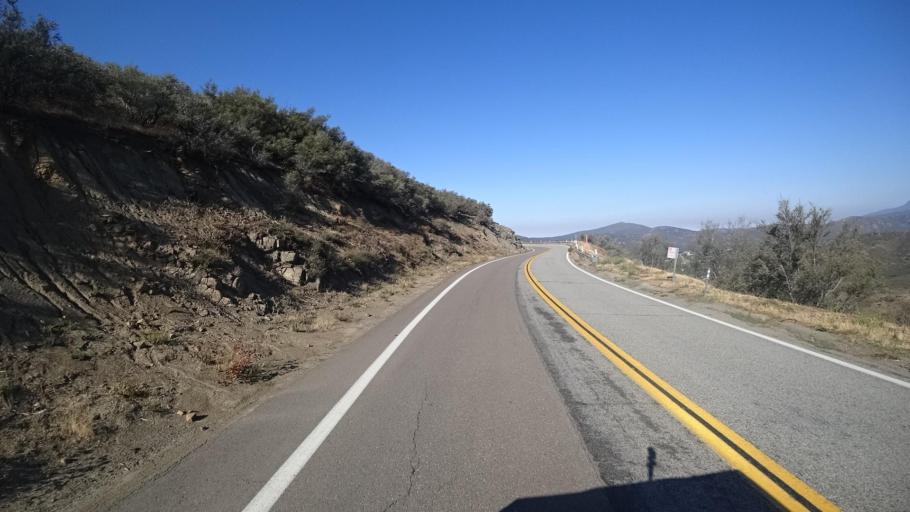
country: US
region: California
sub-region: San Diego County
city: Pine Valley
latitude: 32.8221
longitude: -116.5064
